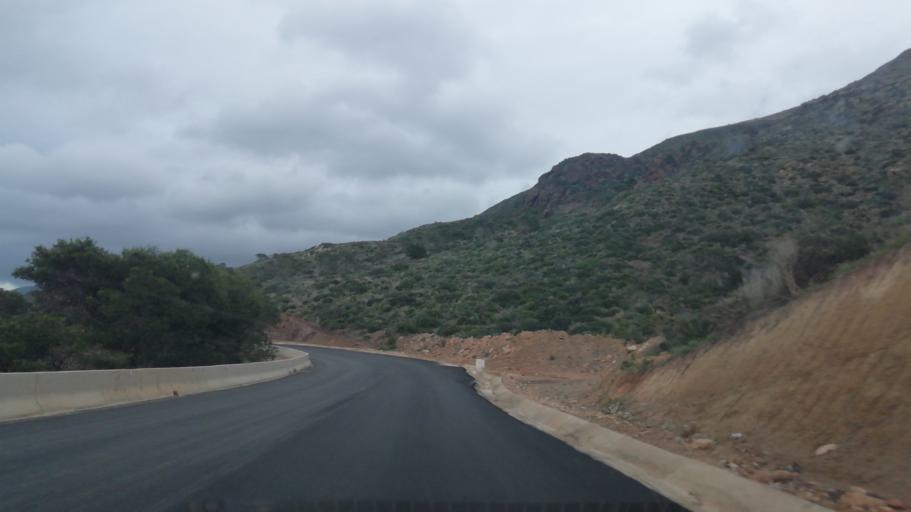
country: DZ
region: Oran
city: Bir el Djir
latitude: 35.7749
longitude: -0.5140
